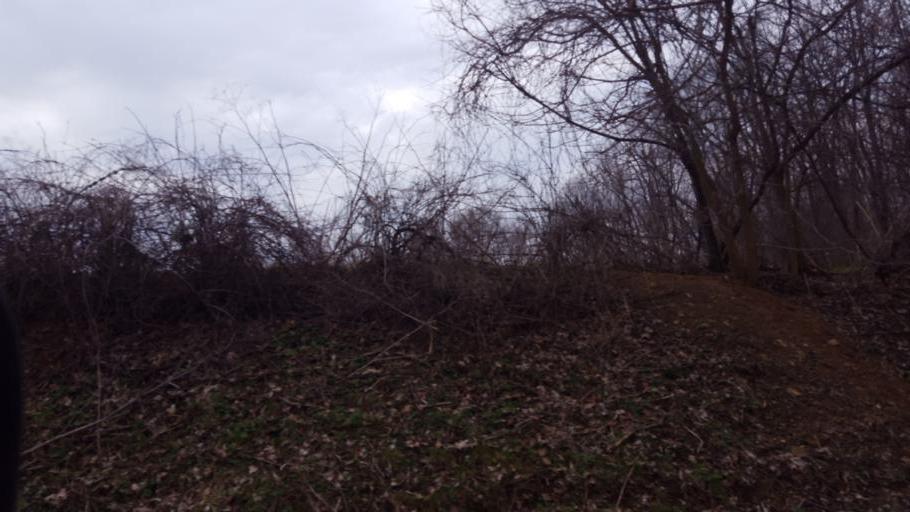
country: US
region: Ohio
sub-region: Ashland County
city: Loudonville
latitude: 40.7192
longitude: -82.3440
